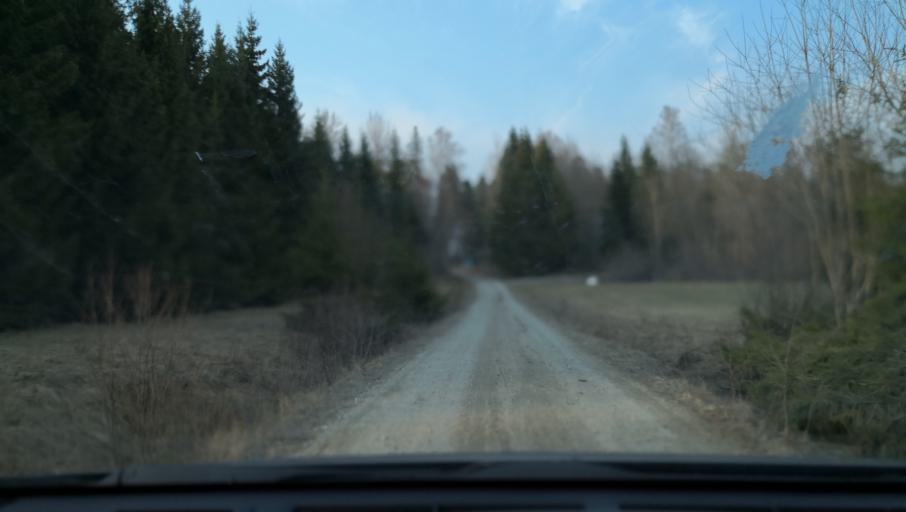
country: SE
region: OErebro
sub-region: Orebro Kommun
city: Hovsta
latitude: 59.3919
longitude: 15.2707
